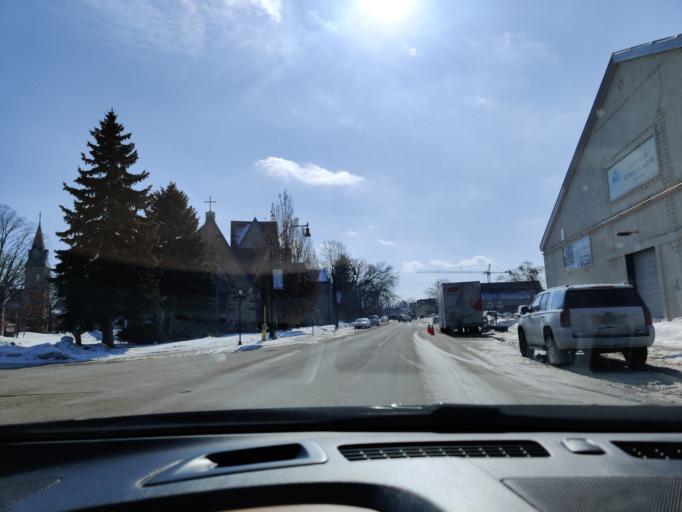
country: CA
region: Ontario
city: Collingwood
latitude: 44.5007
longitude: -80.2154
